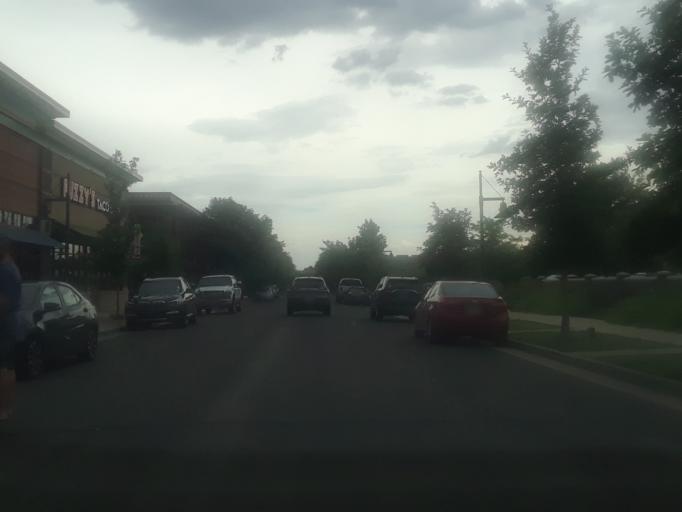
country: US
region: Colorado
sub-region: Broomfield County
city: Broomfield
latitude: 39.9129
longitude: -105.0430
